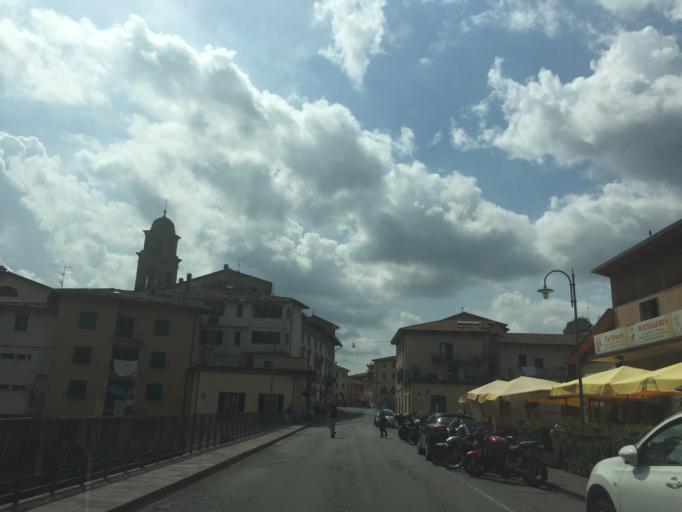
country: IT
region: Tuscany
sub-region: Provincia di Pistoia
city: San Marcello Pistoiese
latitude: 44.0560
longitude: 10.7928
